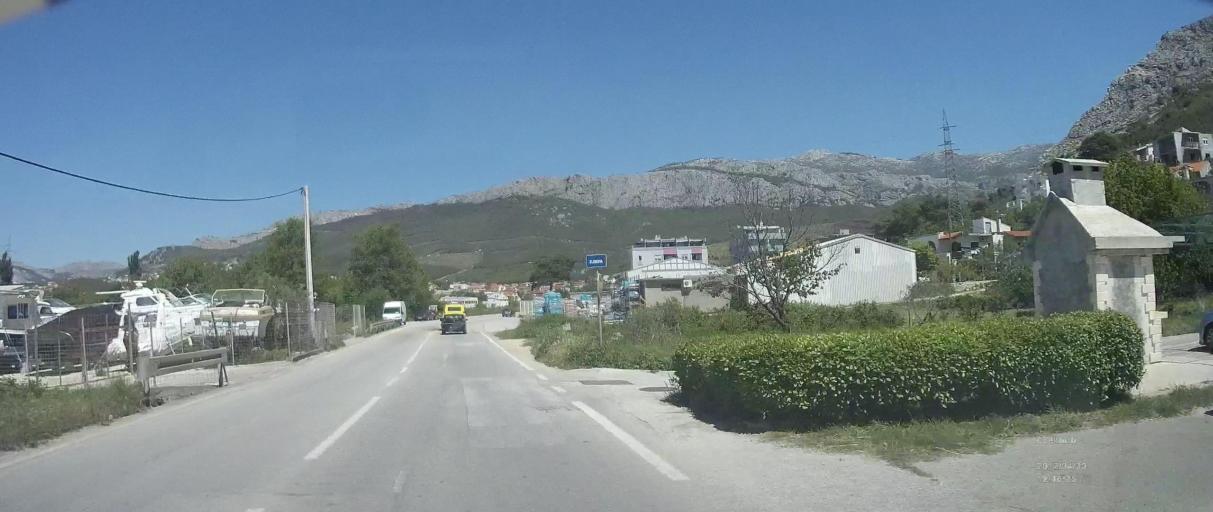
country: HR
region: Splitsko-Dalmatinska
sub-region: Grad Split
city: Stobrec
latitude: 43.5114
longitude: 16.5392
